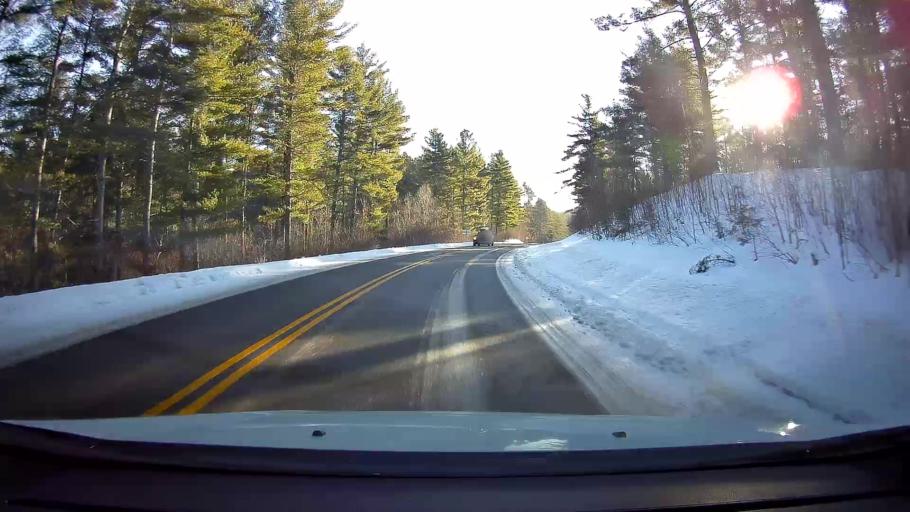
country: US
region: Wisconsin
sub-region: Sawyer County
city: Little Round Lake
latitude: 46.1115
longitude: -91.3071
